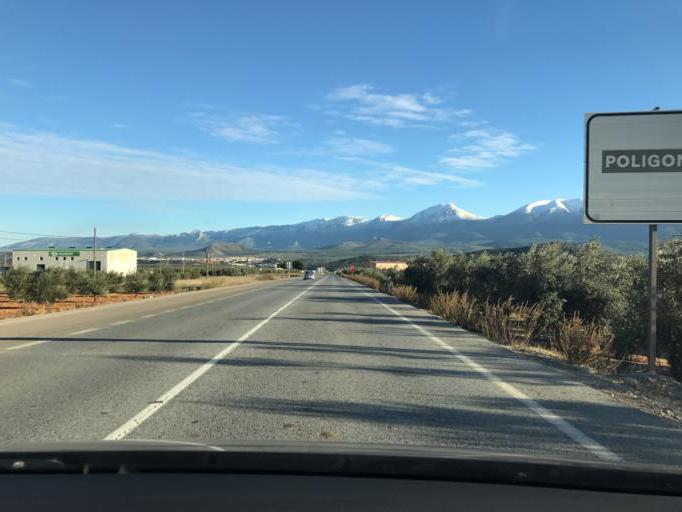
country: ES
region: Andalusia
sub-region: Provincia de Granada
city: Iznalloz
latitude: 37.4037
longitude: -3.5602
